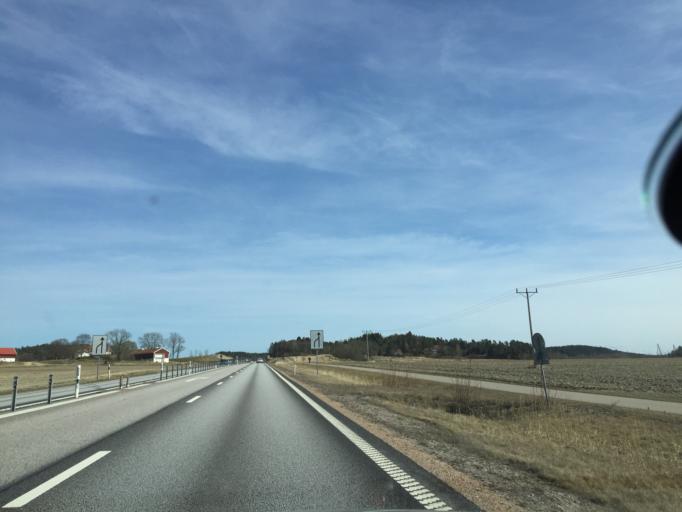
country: SE
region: Vaestra Goetaland
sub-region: Orust
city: Henan
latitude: 58.3457
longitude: 11.7734
